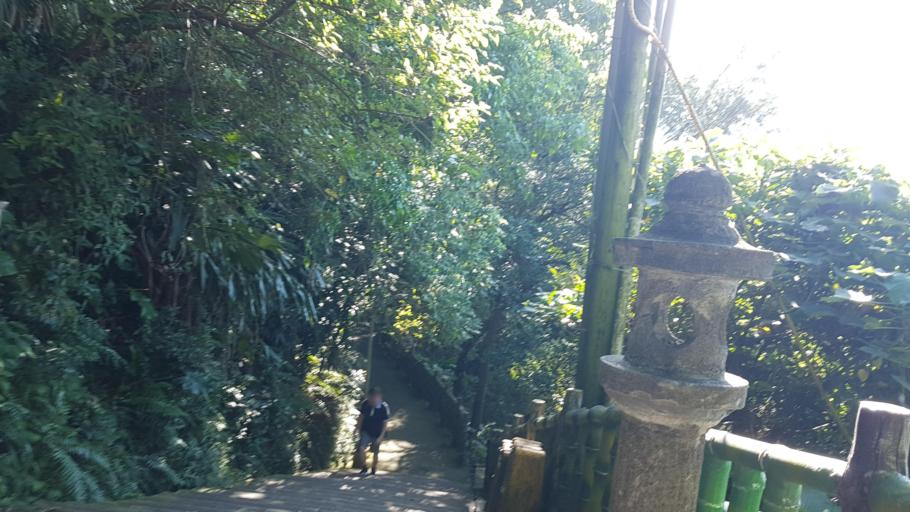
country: TW
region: Taipei
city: Taipei
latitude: 24.9924
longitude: 121.5476
